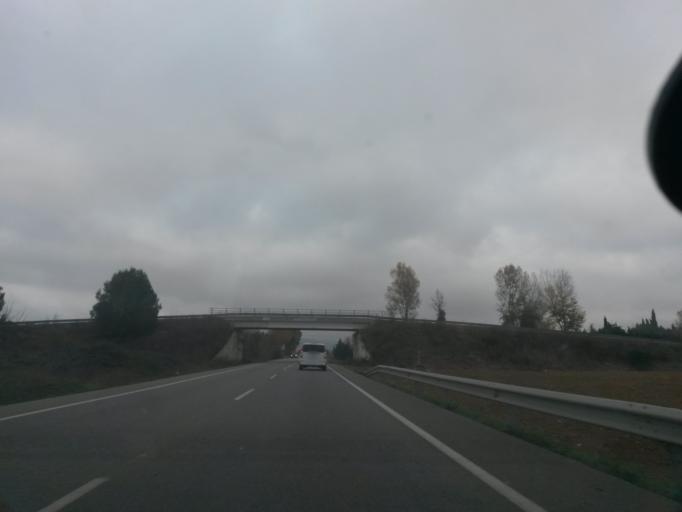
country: ES
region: Catalonia
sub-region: Provincia de Girona
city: Banyoles
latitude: 42.1454
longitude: 2.7629
